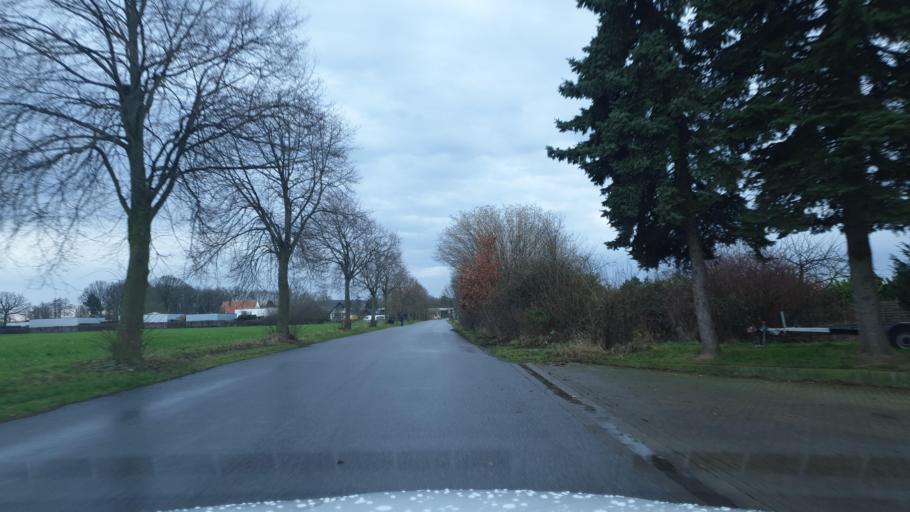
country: DE
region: North Rhine-Westphalia
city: Bad Oeynhausen
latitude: 52.1789
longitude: 8.8098
